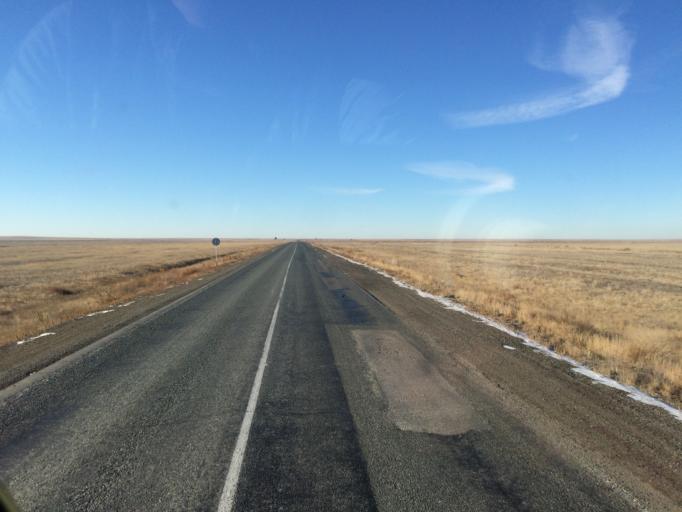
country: KZ
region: Aqtoebe
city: Khromtau
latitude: 50.1845
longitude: 58.6637
